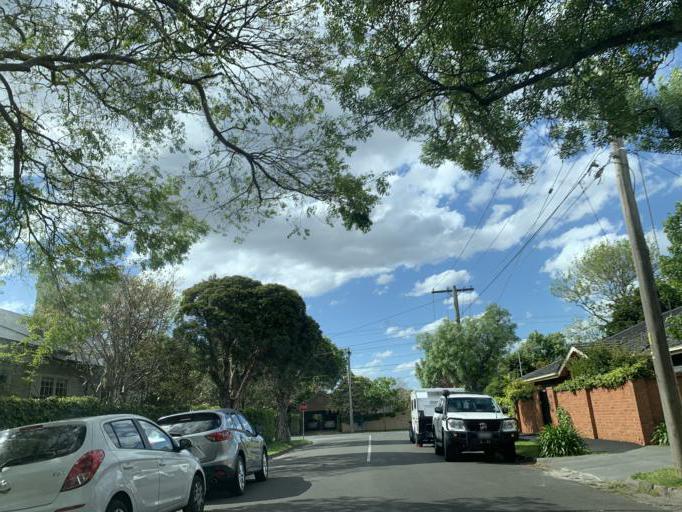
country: AU
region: Victoria
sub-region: Bayside
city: North Brighton
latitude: -37.9212
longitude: 145.0044
